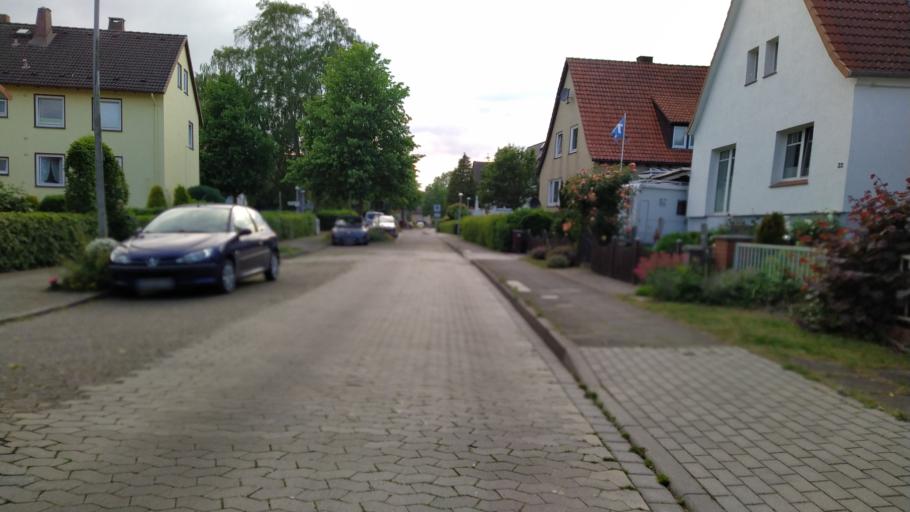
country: DE
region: Lower Saxony
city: Buxtehude
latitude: 53.4743
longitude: 9.6893
